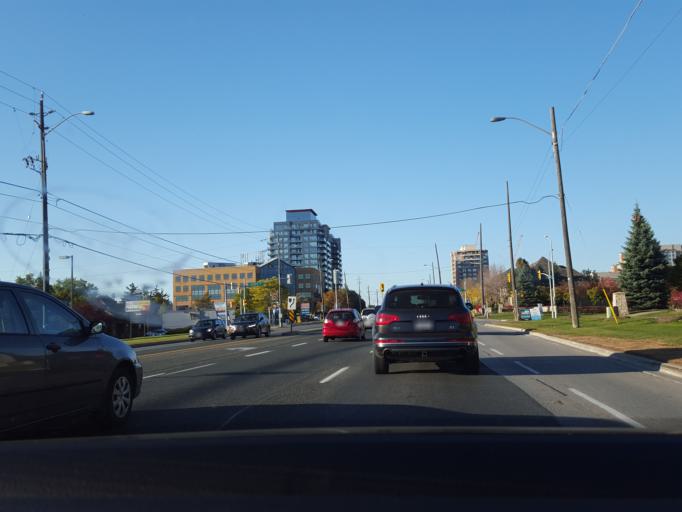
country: CA
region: Ontario
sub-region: York
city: Richmond Hill
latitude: 43.8455
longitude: -79.4311
